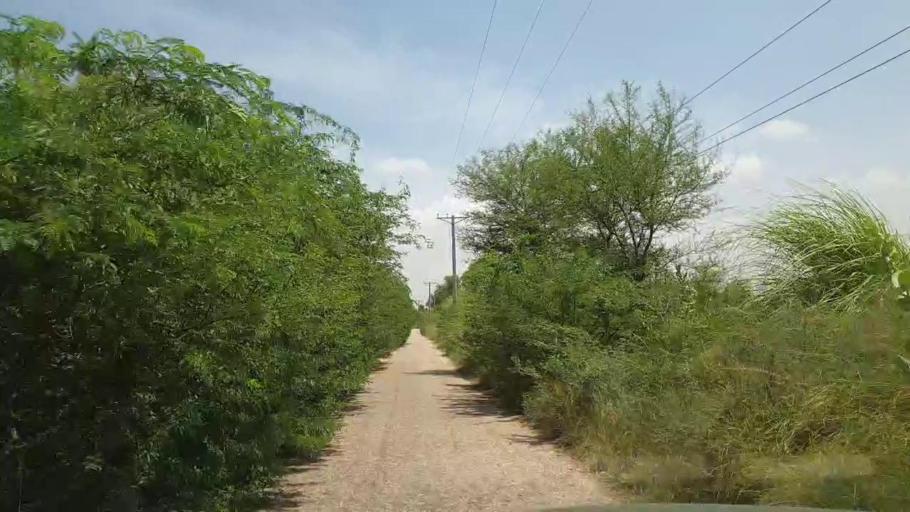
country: PK
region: Sindh
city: Kot Diji
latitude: 27.1347
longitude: 69.0065
